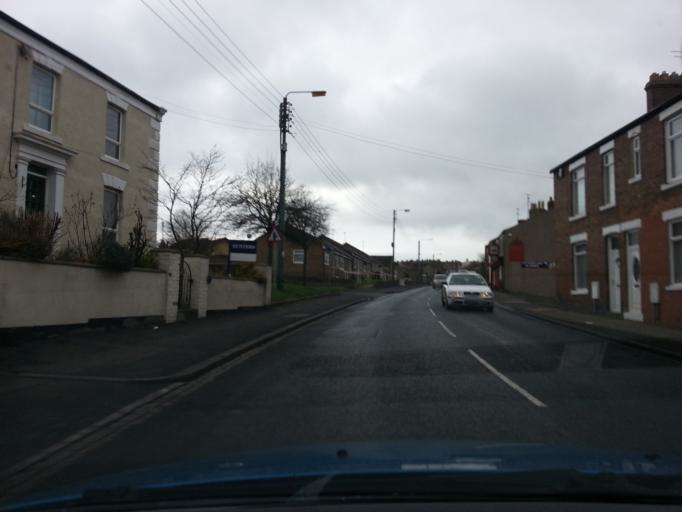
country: GB
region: England
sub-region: County Durham
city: Crook
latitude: 54.7133
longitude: -1.7382
